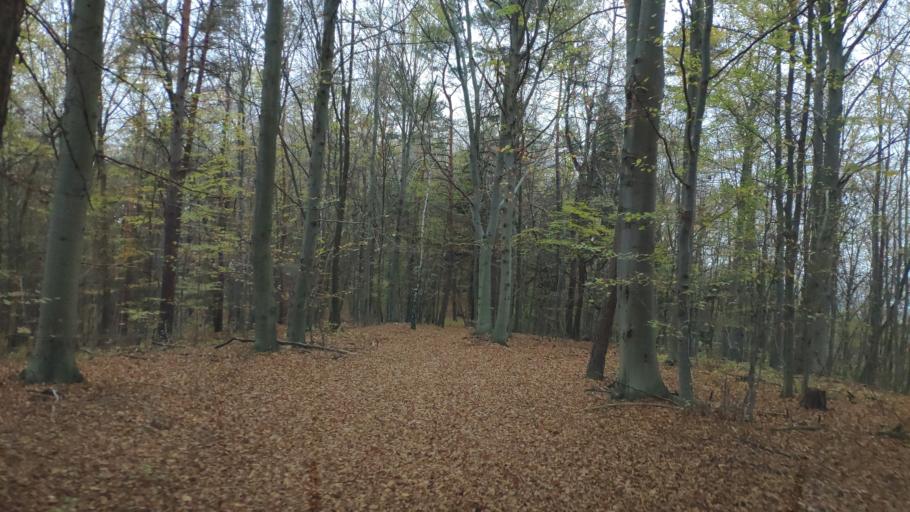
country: SK
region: Presovsky
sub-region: Okres Presov
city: Presov
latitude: 48.9401
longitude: 21.1026
